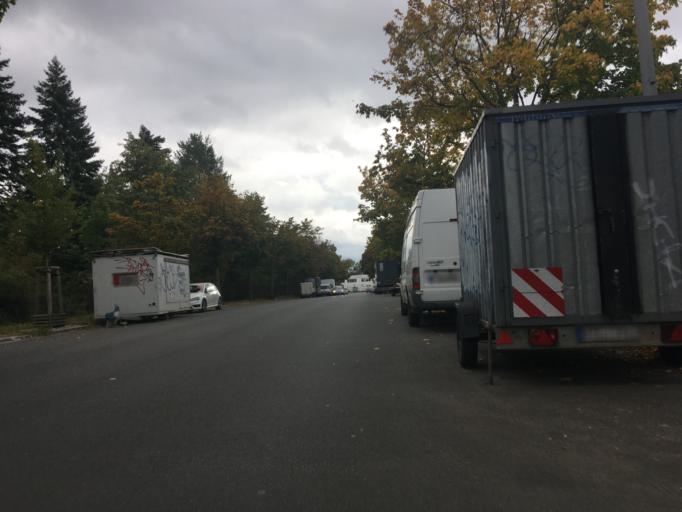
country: DE
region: Berlin
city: Tempelhof Bezirk
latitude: 52.4547
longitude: 13.3999
